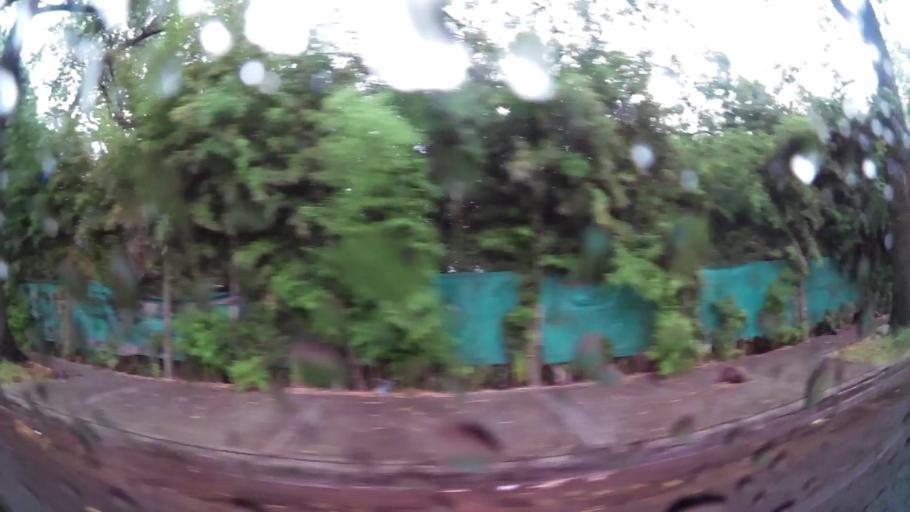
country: AR
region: Buenos Aires F.D.
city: Buenos Aires
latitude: -34.6266
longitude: -58.3644
